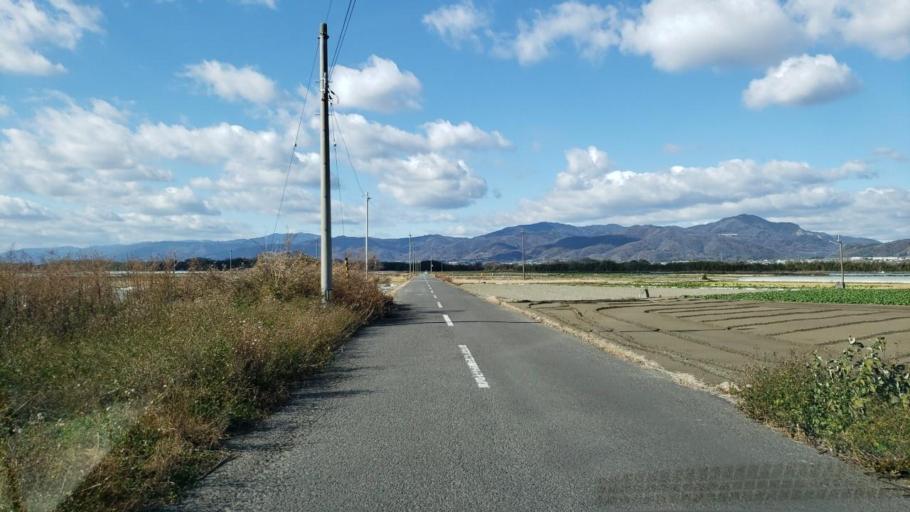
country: JP
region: Tokushima
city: Kamojimacho-jogejima
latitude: 34.0707
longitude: 134.3043
